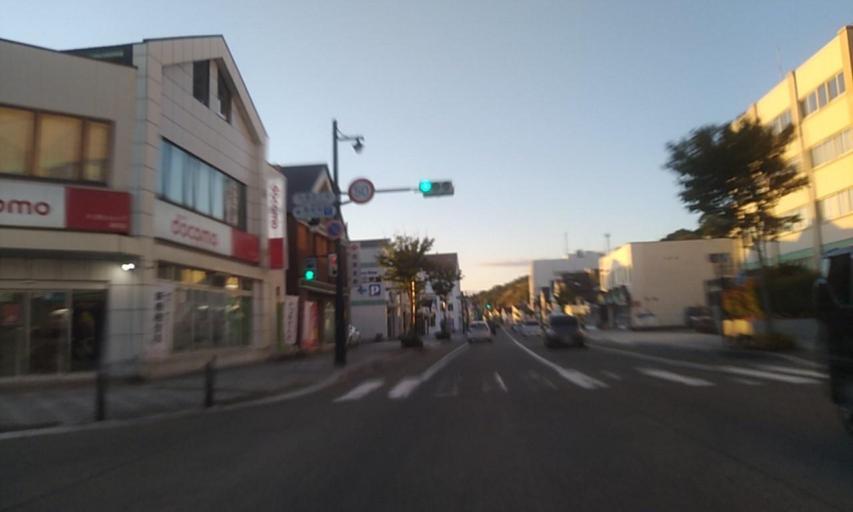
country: JP
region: Hokkaido
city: Shizunai-furukawacho
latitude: 42.1623
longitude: 142.7748
